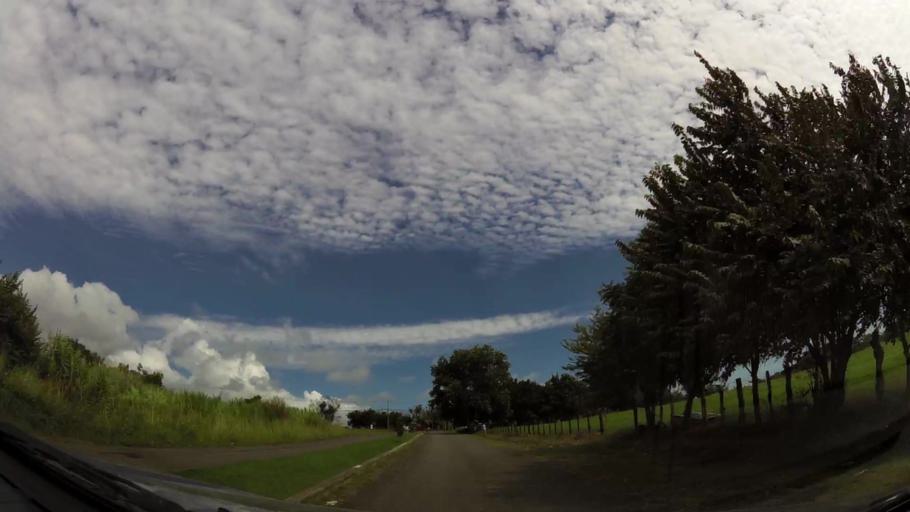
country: PA
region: Panama
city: Nueva Gorgona
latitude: 8.5374
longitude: -79.9079
